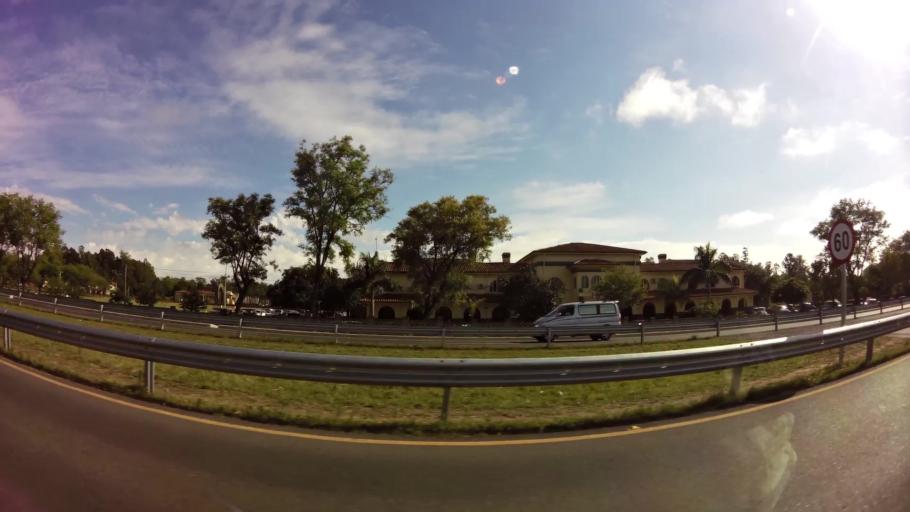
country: PY
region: Central
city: Fernando de la Mora
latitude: -25.2576
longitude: -57.5462
